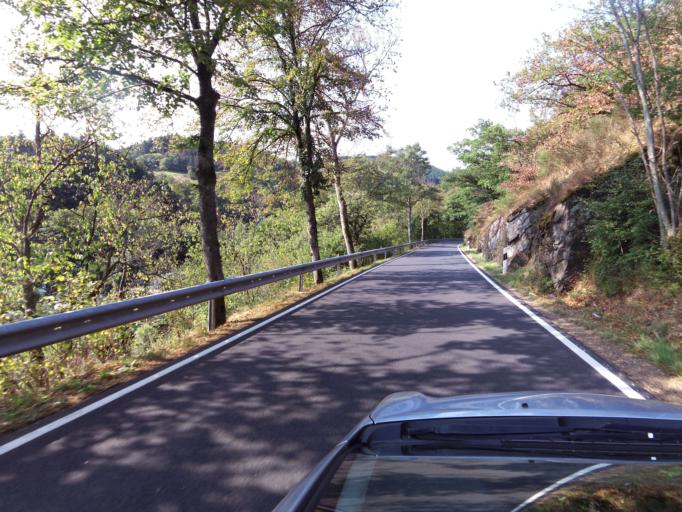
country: LU
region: Diekirch
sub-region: Canton de Wiltz
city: Goesdorf
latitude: 49.9063
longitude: 5.9564
